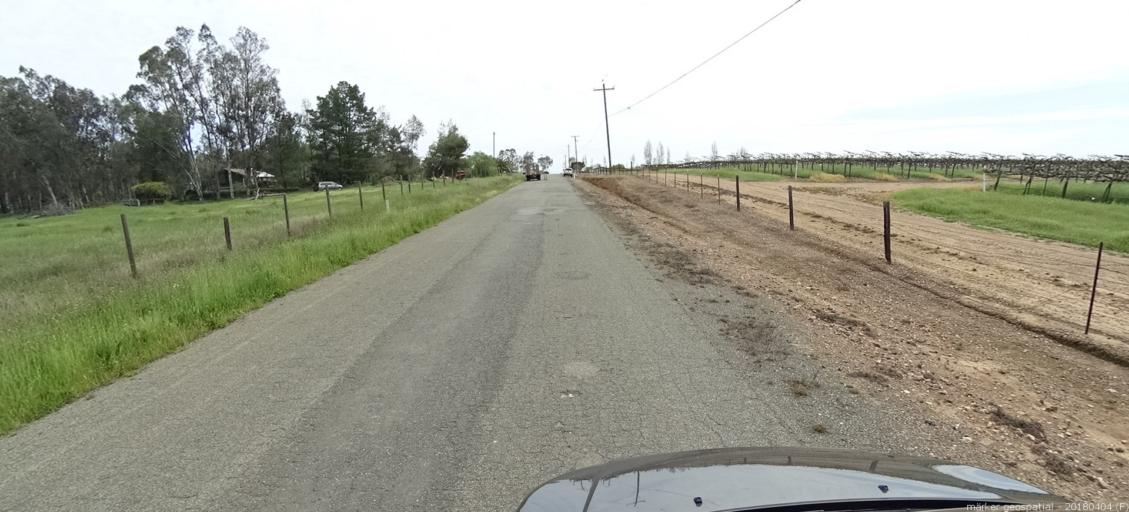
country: US
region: California
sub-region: Sacramento County
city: Clay
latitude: 38.2929
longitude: -121.1597
